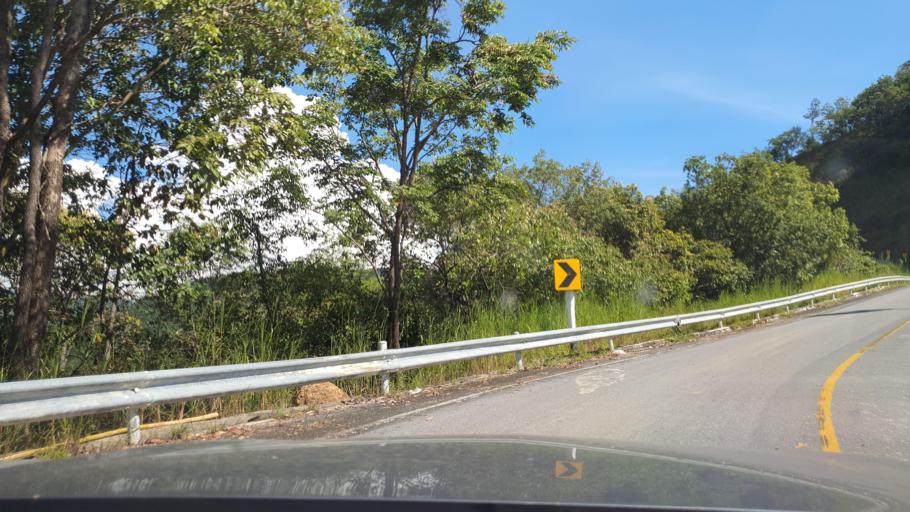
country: TH
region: Chiang Mai
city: Phrao
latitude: 19.3623
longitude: 99.2722
